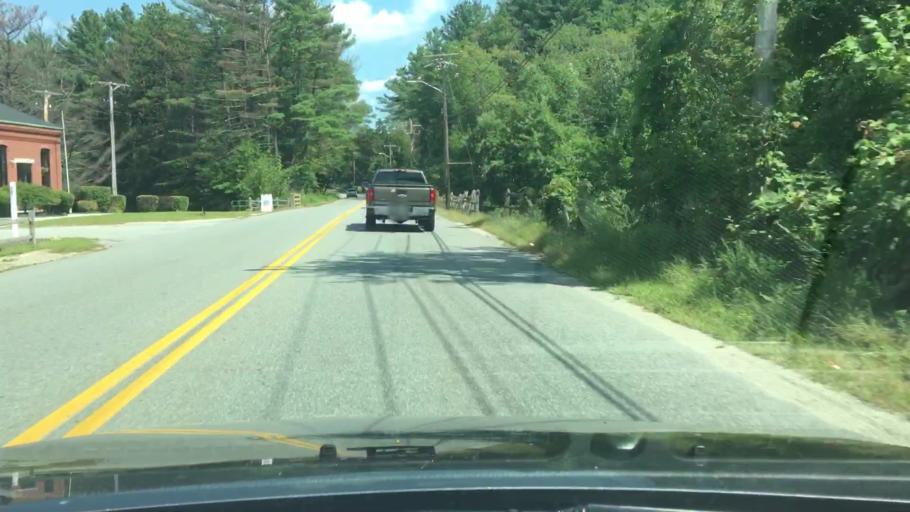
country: US
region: Massachusetts
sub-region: Worcester County
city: Milford
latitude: 42.1613
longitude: -71.5125
